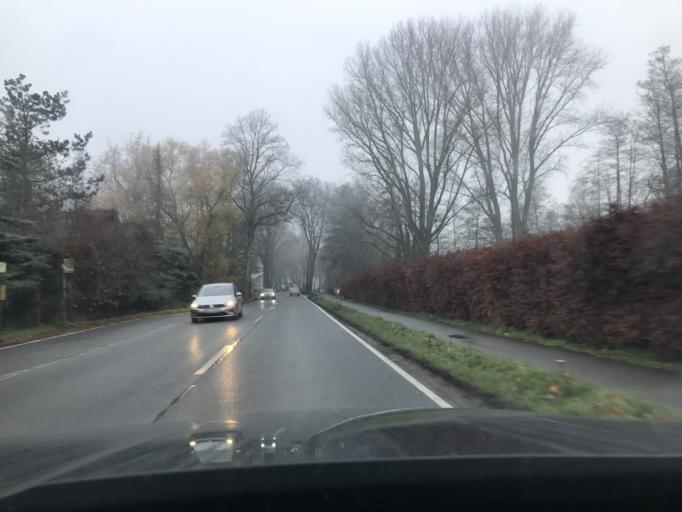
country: DE
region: North Rhine-Westphalia
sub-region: Regierungsbezirk Dusseldorf
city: Nettetal
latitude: 51.2809
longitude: 6.2710
